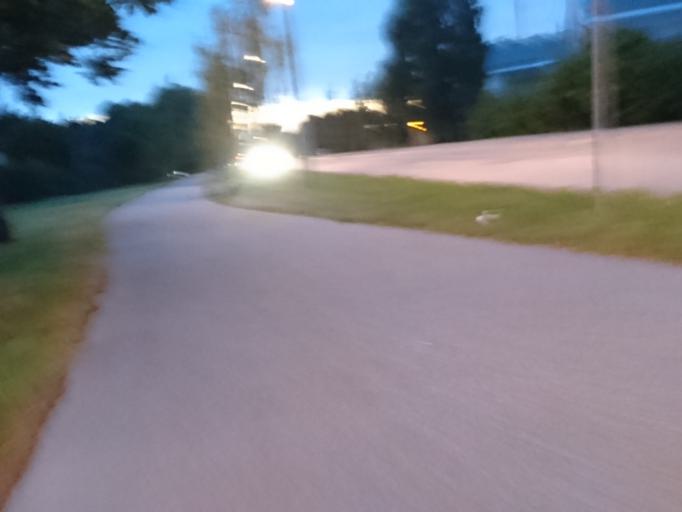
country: SE
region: Stockholm
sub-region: Huddinge Kommun
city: Huddinge
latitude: 59.2747
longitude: 17.9855
